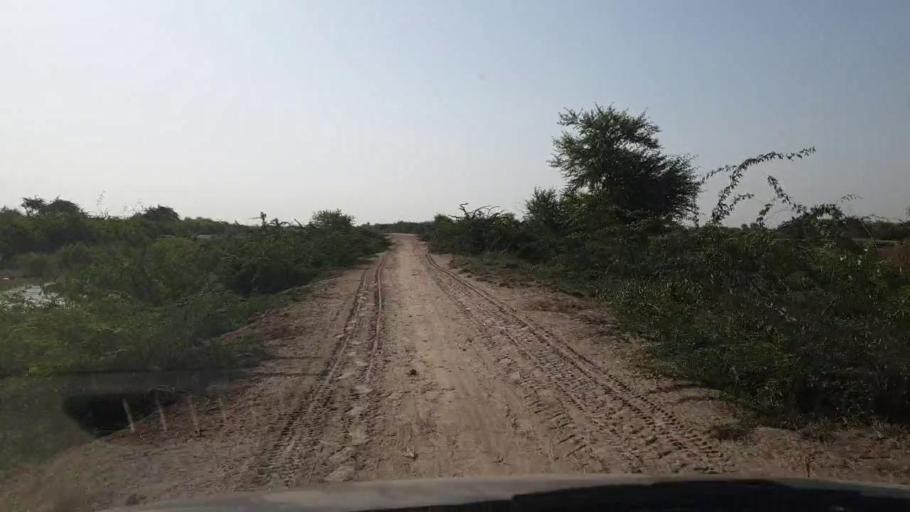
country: PK
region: Sindh
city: Kadhan
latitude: 24.5937
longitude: 69.0759
